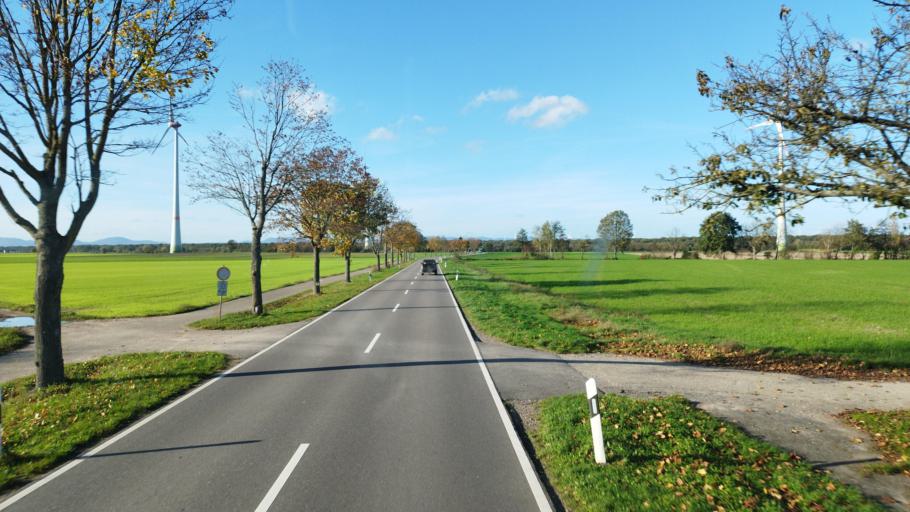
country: DE
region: Rheinland-Pfalz
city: Hatzenbuhl
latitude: 49.1172
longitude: 8.2397
